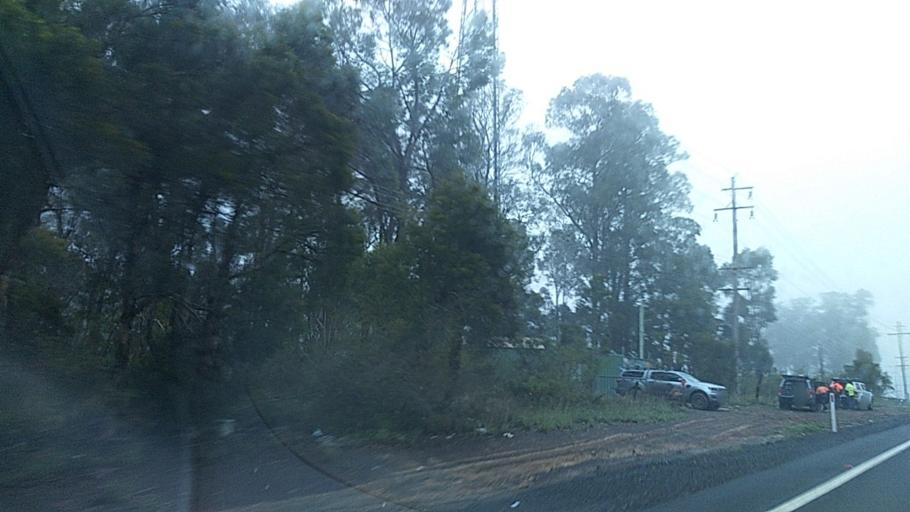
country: AU
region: New South Wales
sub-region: Hawkesbury
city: South Windsor
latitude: -33.6630
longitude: 150.7608
